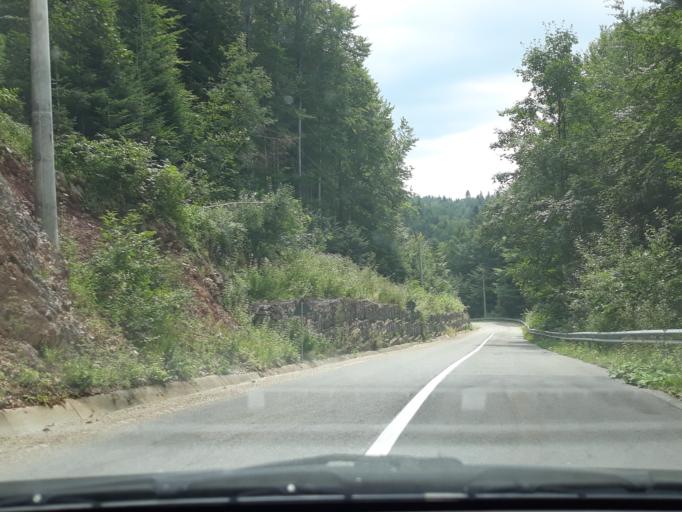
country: RO
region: Bihor
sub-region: Comuna Pietroasa
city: Pietroasa
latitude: 46.5911
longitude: 22.6756
